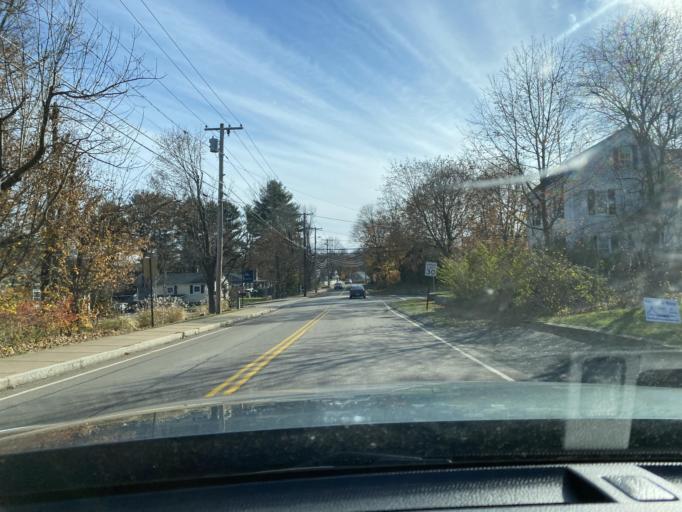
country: US
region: Massachusetts
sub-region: Norfolk County
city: Medfield
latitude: 42.1837
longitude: -71.2992
